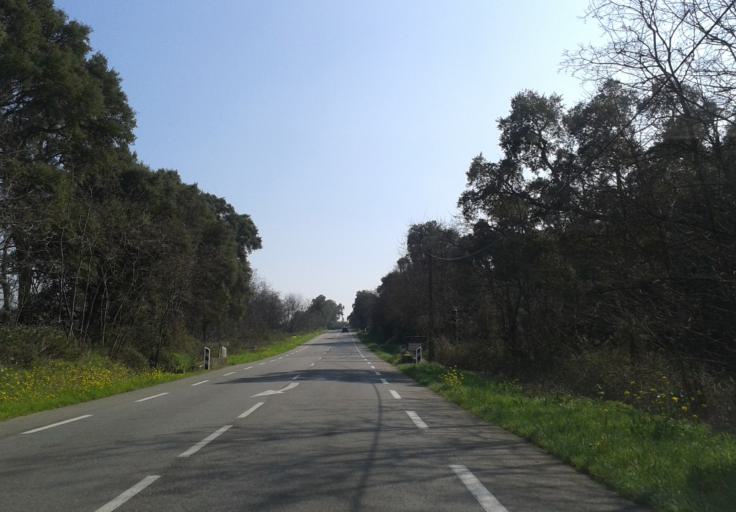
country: FR
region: Corsica
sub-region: Departement de la Haute-Corse
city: Cervione
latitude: 42.3002
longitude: 9.5449
